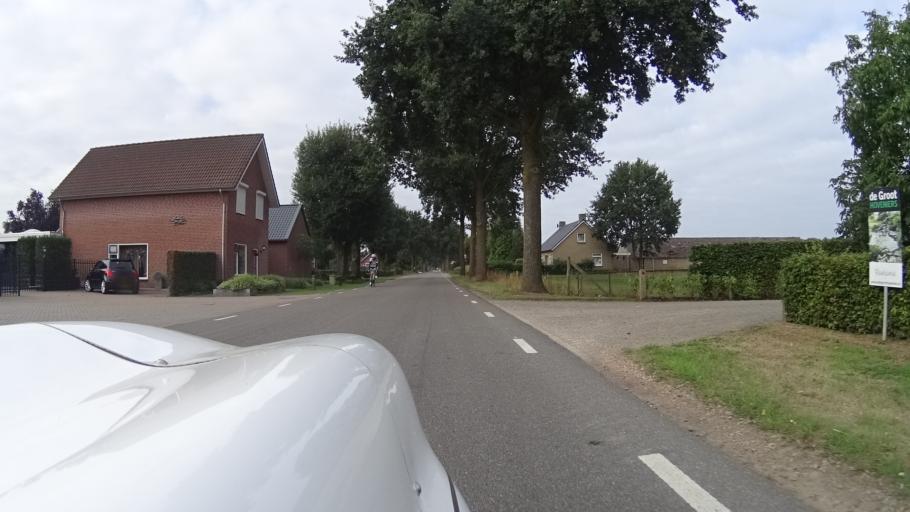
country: NL
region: North Brabant
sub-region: Gemeente Boxmeer
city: Overloon
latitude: 51.5857
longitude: 5.9413
